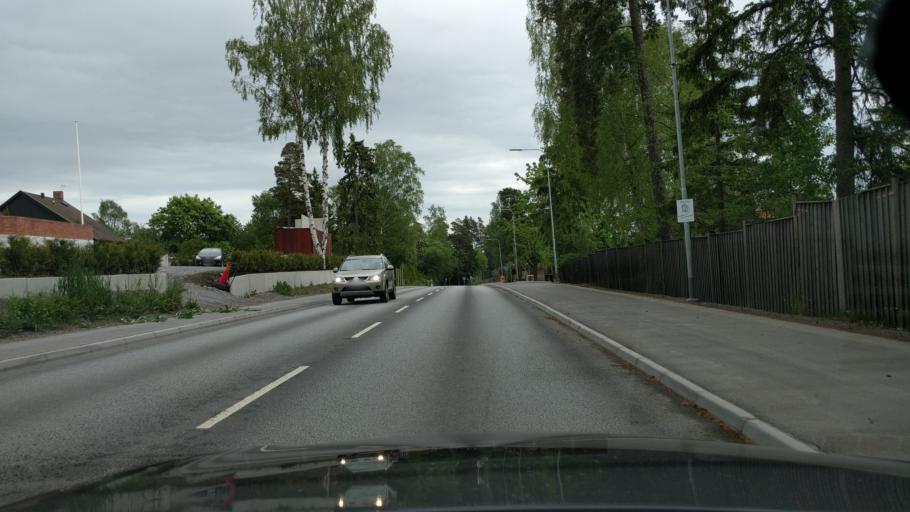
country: SE
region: Stockholm
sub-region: Taby Kommun
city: Taby
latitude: 59.4548
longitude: 18.0389
